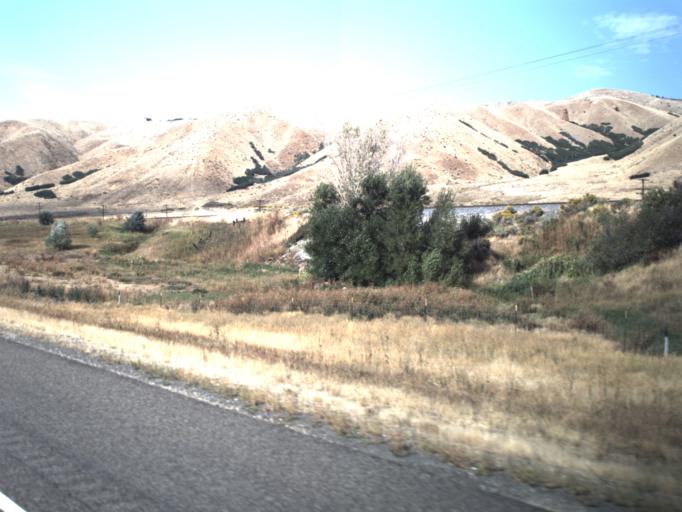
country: US
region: Utah
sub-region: Summit County
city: Coalville
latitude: 40.9835
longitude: -111.4490
